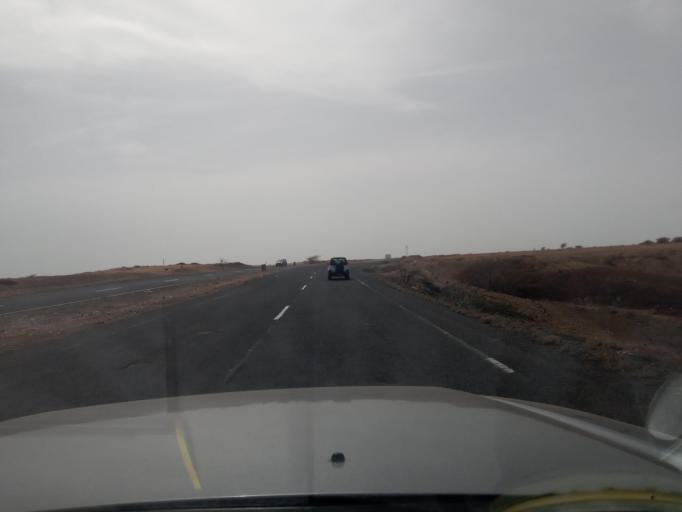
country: CV
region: Sal
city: Santa Maria
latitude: 16.6444
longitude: -22.9171
